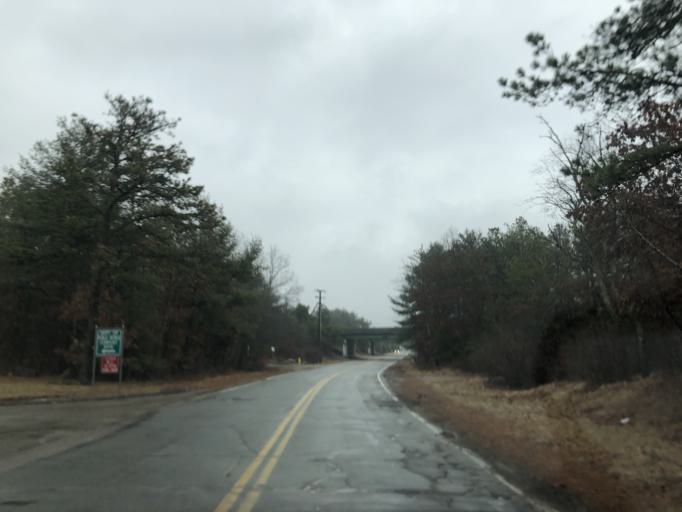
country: US
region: Massachusetts
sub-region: Norfolk County
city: Plainville
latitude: 42.0065
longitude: -71.2872
